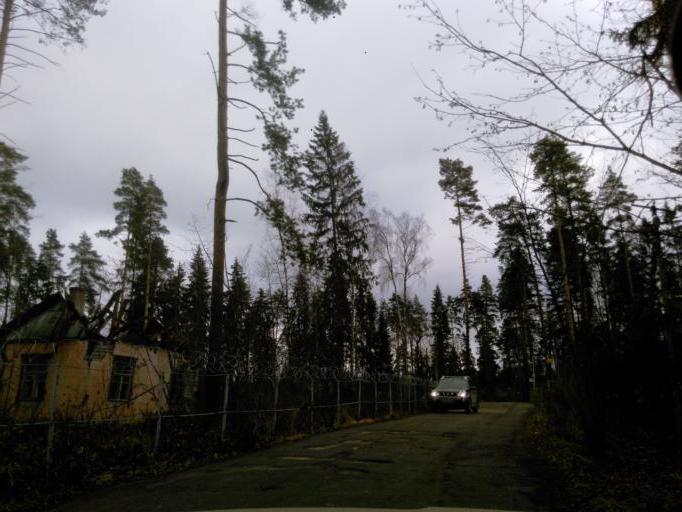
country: RU
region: Moskovskaya
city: Lozhki
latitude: 56.0530
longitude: 37.0999
